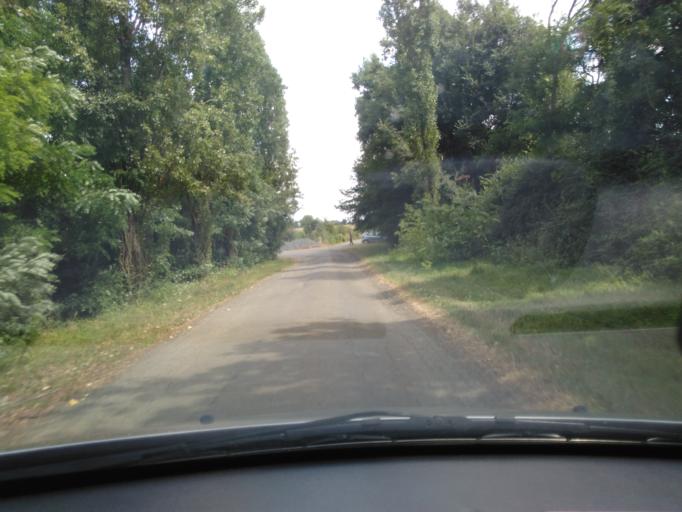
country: FR
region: Pays de la Loire
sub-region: Departement de la Vendee
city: Sainte-Hermine
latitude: 46.5761
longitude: -1.0250
